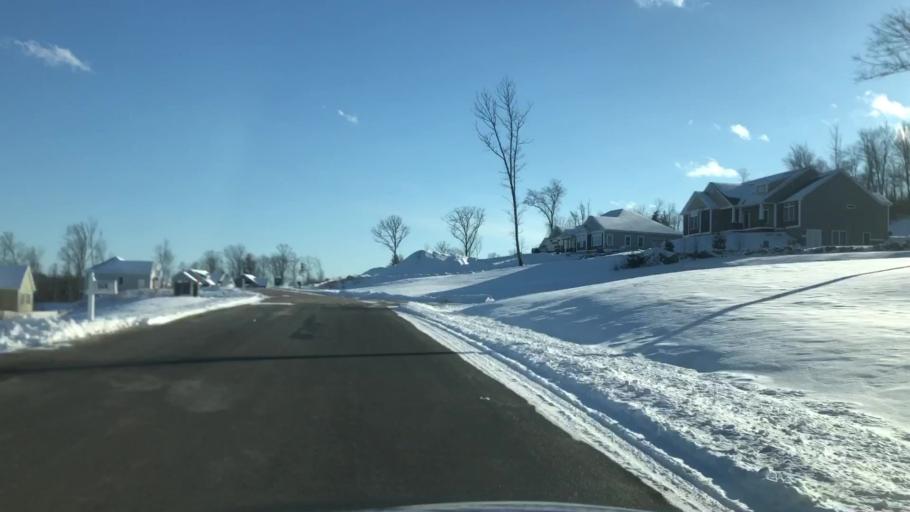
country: US
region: New Hampshire
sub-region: Hillsborough County
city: Wilton
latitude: 42.8068
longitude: -71.7113
